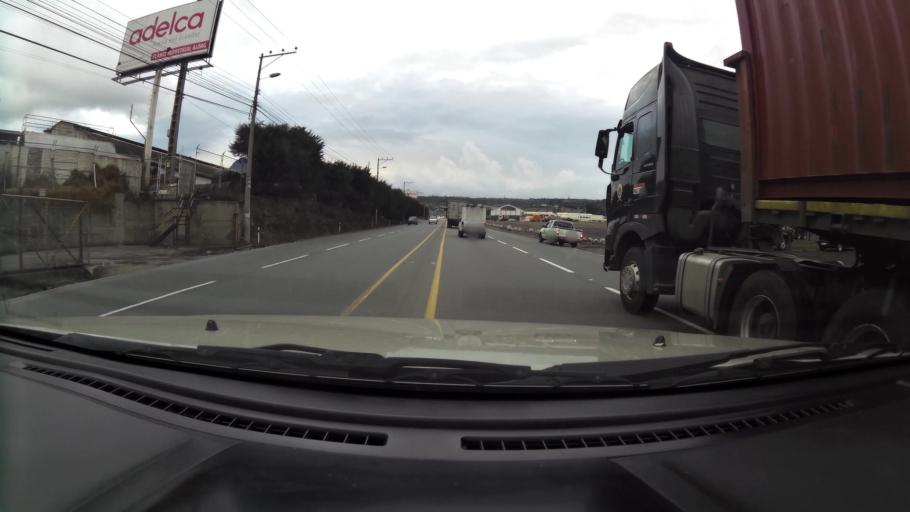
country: EC
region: Pichincha
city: Machachi
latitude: -0.4477
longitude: -78.6346
